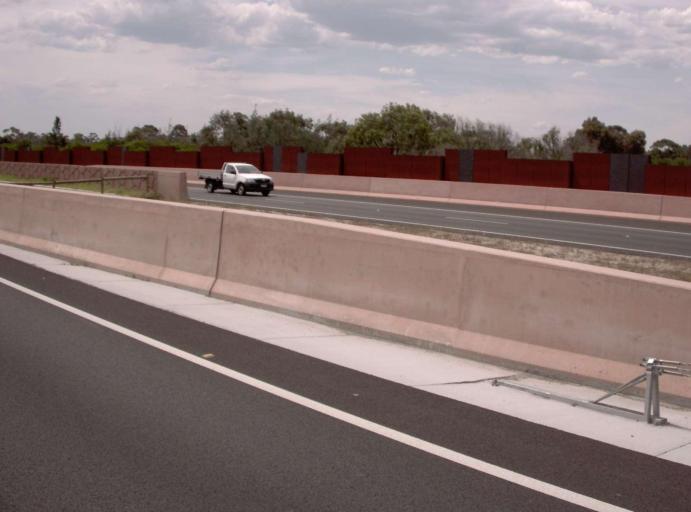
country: AU
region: Victoria
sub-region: Frankston
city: Carrum Downs
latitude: -38.1186
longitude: 145.1696
